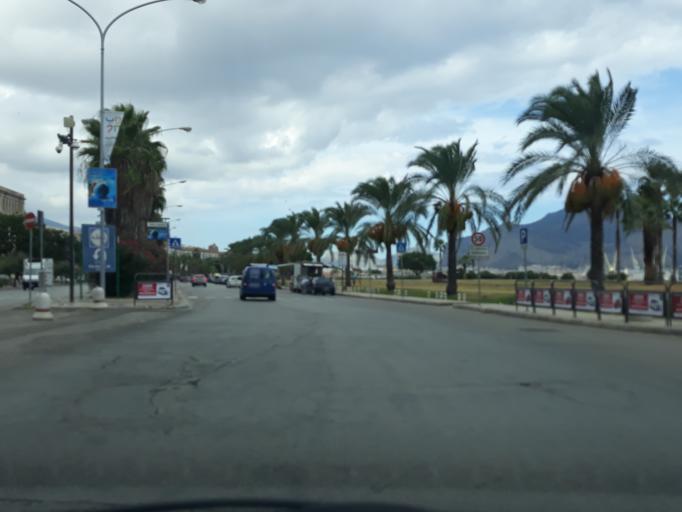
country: IT
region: Sicily
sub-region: Palermo
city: Palermo
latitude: 38.1151
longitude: 13.3765
